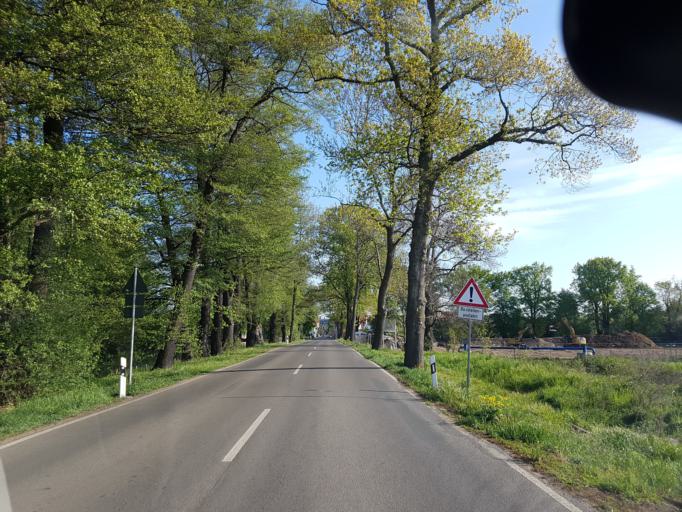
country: DE
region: Brandenburg
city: Altdobern
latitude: 51.6478
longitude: 14.0343
